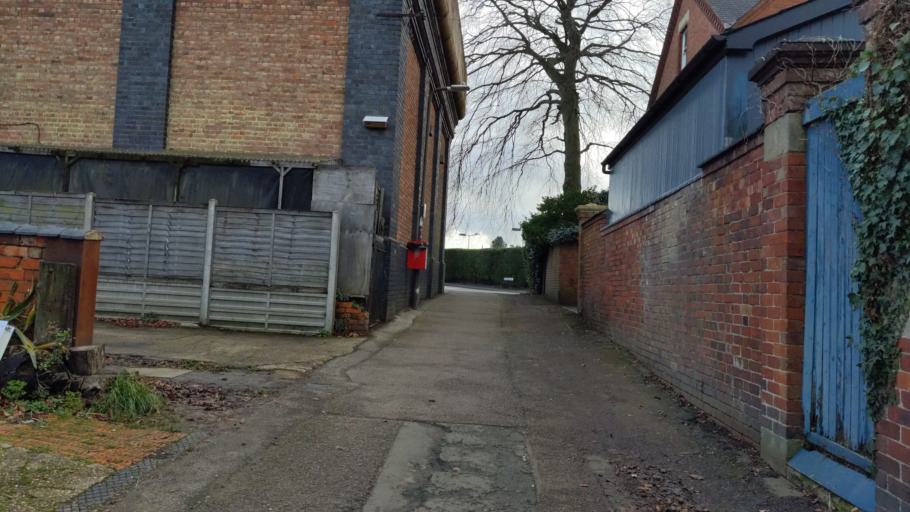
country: GB
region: England
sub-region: Milton Keynes
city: Bradwell
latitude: 52.0593
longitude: -0.8122
